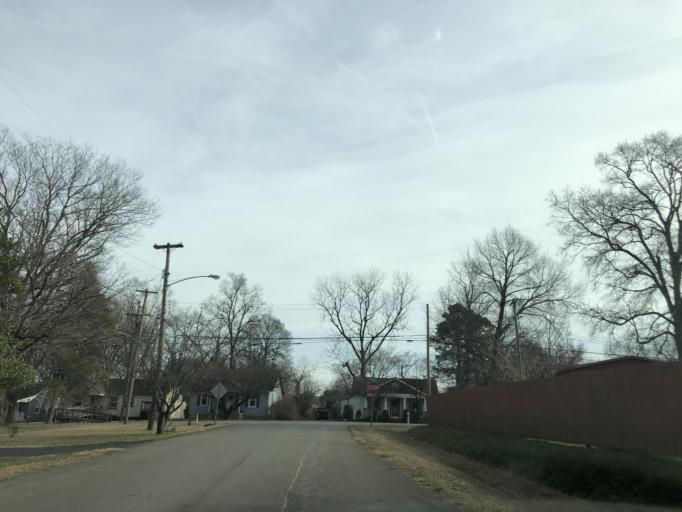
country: US
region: Tennessee
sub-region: Davidson County
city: Nashville
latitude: 36.2169
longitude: -86.7336
